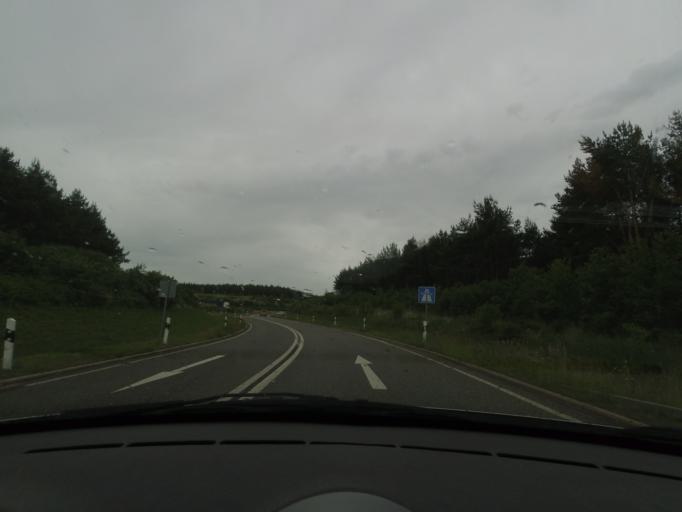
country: DE
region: Thuringia
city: Hermsdorf
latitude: 50.8898
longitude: 11.8484
